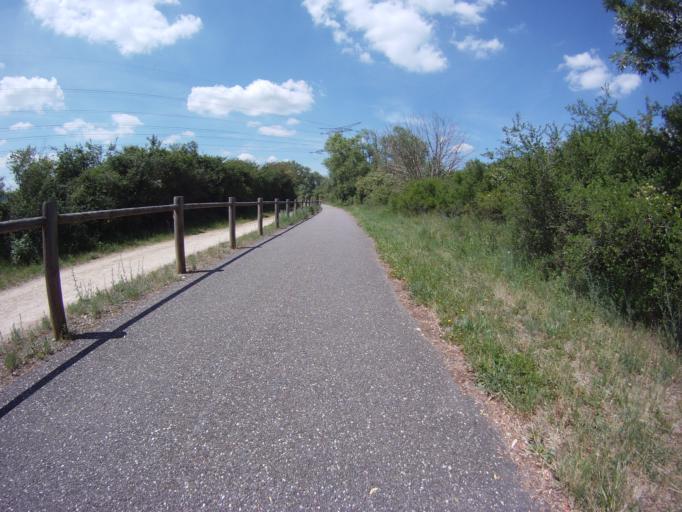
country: FR
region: Lorraine
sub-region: Departement de Meurthe-et-Moselle
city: Eulmont
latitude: 48.7408
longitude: 6.2481
